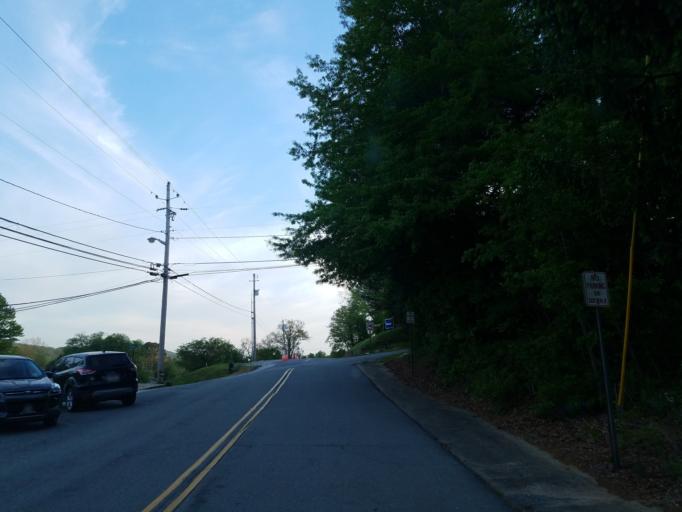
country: US
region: Georgia
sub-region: Fannin County
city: Blue Ridge
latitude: 34.8642
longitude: -84.3277
